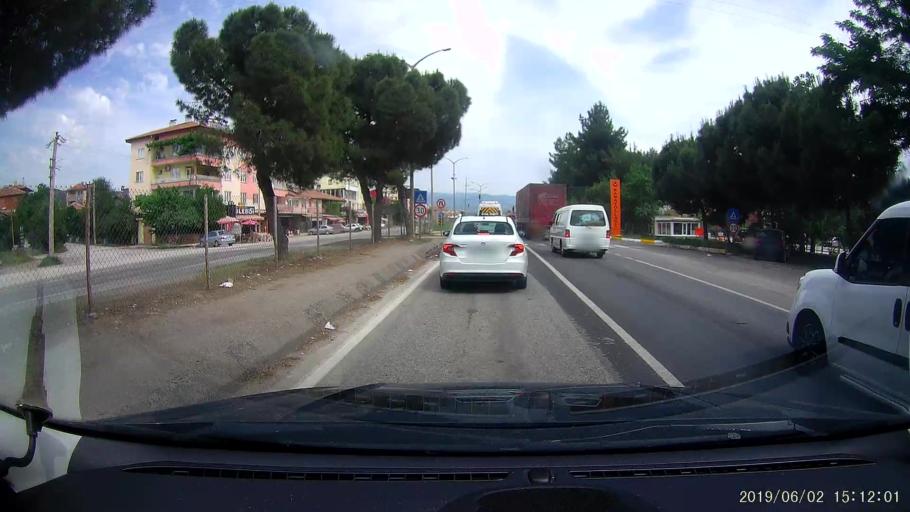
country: TR
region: Corum
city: Osmancik
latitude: 40.9771
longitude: 34.8101
